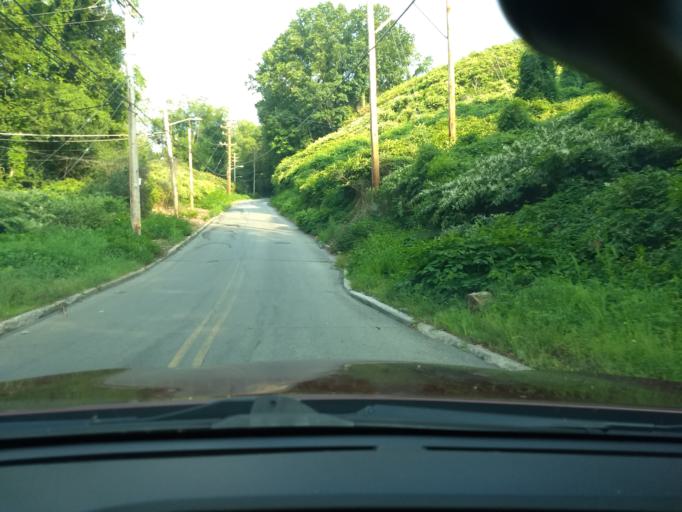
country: US
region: Pennsylvania
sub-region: Allegheny County
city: Aspinwall
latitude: 40.4739
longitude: -79.9044
